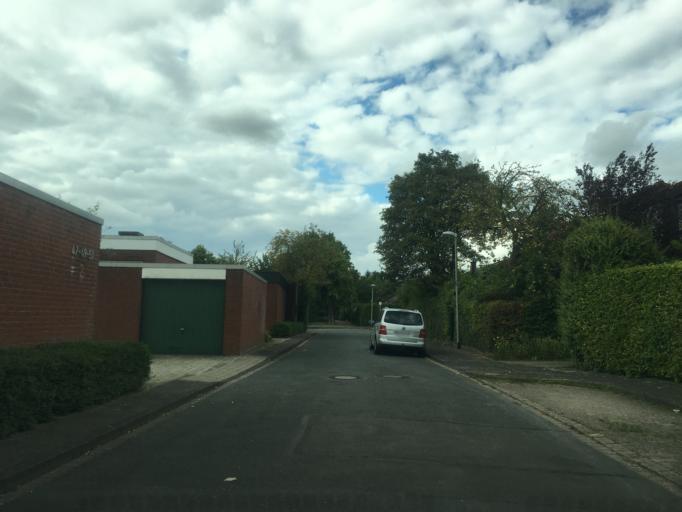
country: DE
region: North Rhine-Westphalia
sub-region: Regierungsbezirk Munster
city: Muenster
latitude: 51.9706
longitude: 7.5790
